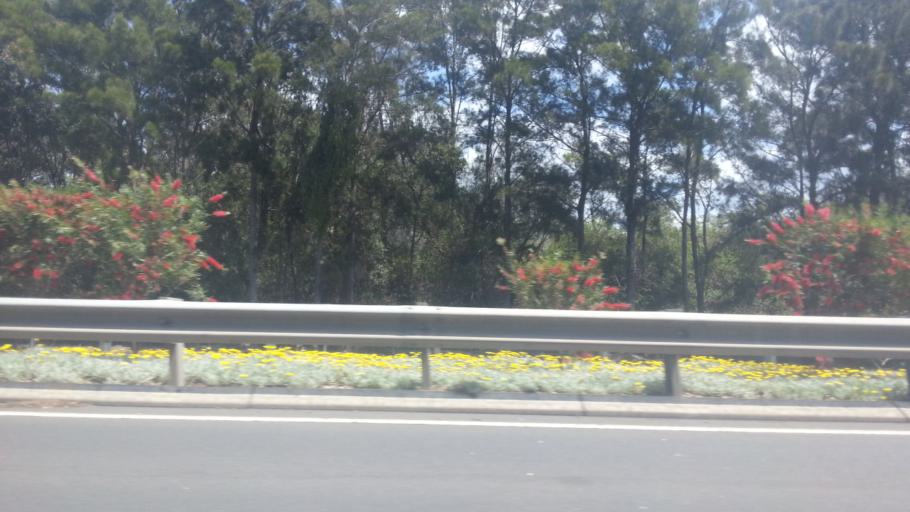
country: AU
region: New South Wales
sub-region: Wollongong
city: Corrimal
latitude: -34.3791
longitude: 150.9006
